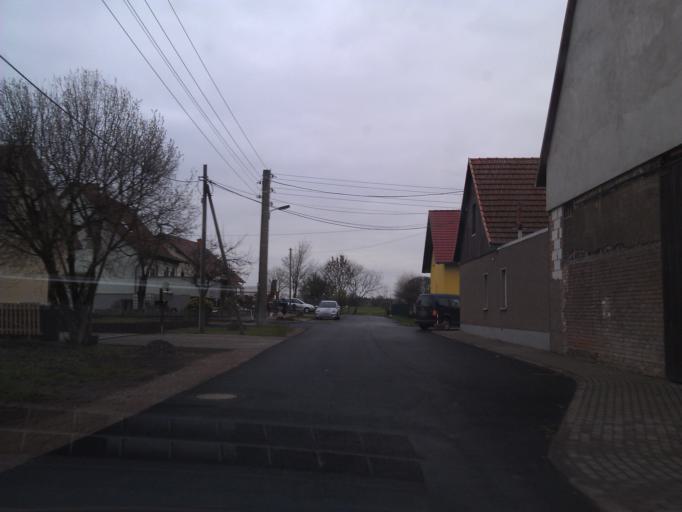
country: DE
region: Thuringia
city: Bufleben
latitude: 50.9985
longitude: 10.7415
